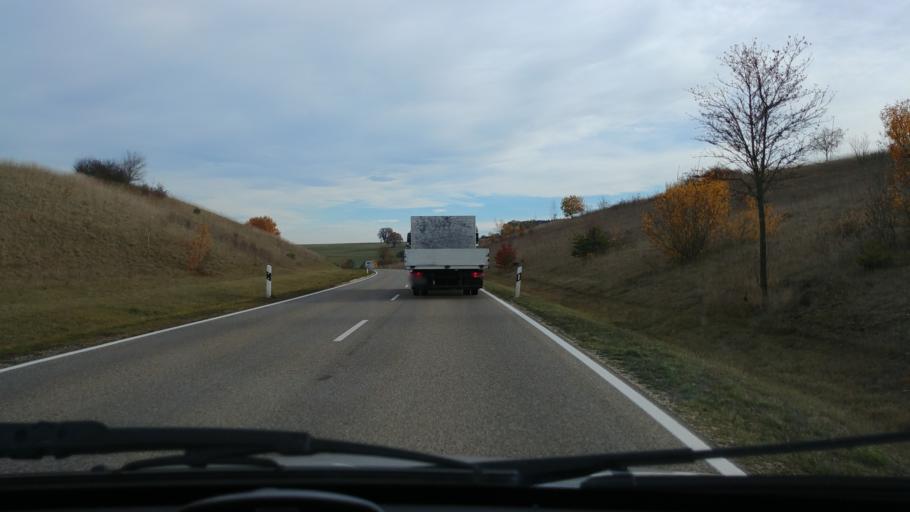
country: DE
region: Baden-Wuerttemberg
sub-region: Regierungsbezirk Stuttgart
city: Giengen an der Brenz
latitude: 48.6548
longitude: 10.2727
